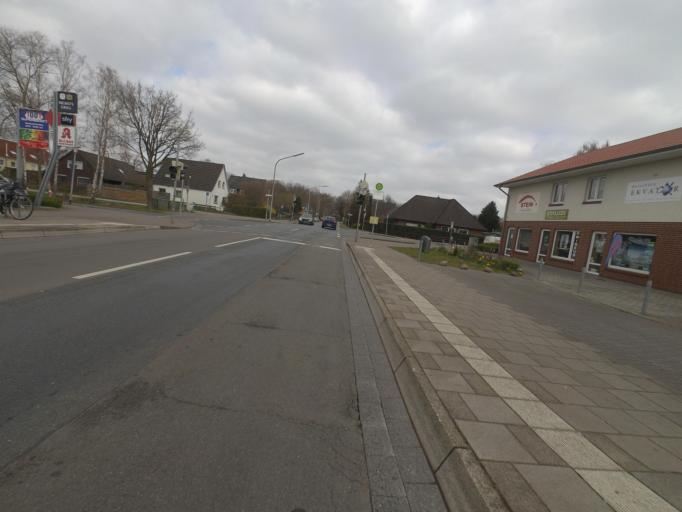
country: DE
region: Lower Saxony
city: Wardenburg
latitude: 53.0959
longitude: 8.2351
